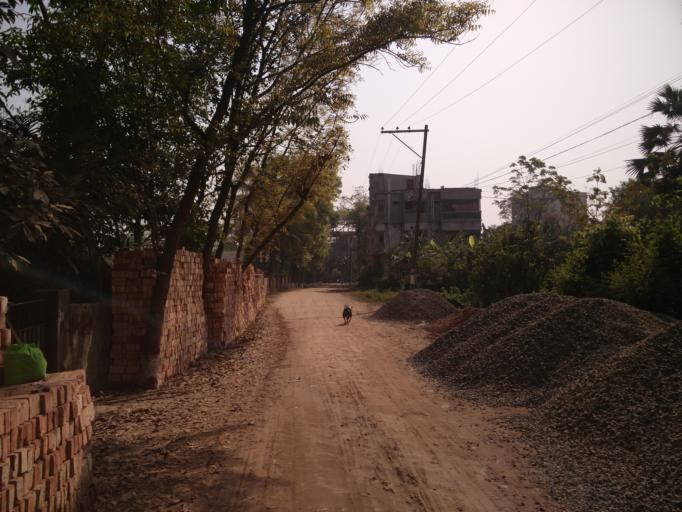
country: BD
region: Dhaka
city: Tungi
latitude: 23.8583
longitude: 90.2549
